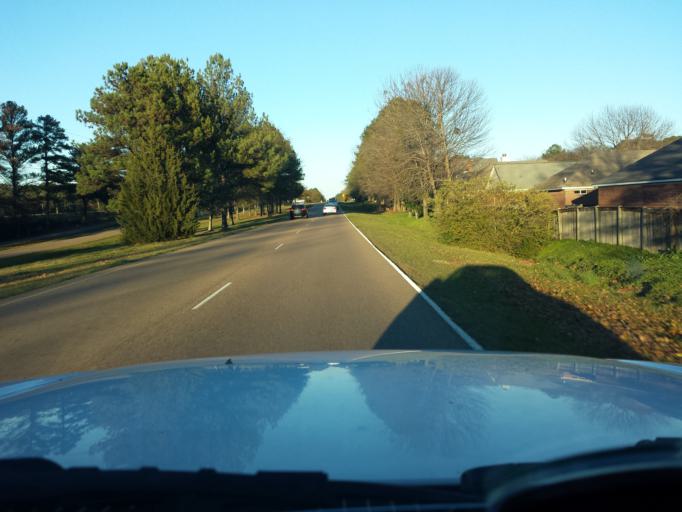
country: US
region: Mississippi
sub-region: Madison County
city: Ridgeland
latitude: 32.3863
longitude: -90.0378
